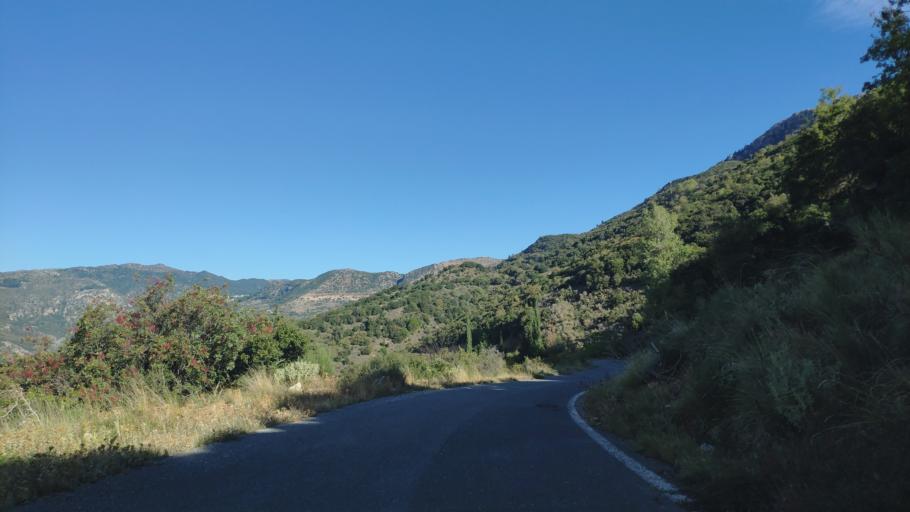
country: GR
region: Peloponnese
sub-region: Nomos Arkadias
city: Dimitsana
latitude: 37.5530
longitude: 22.0603
